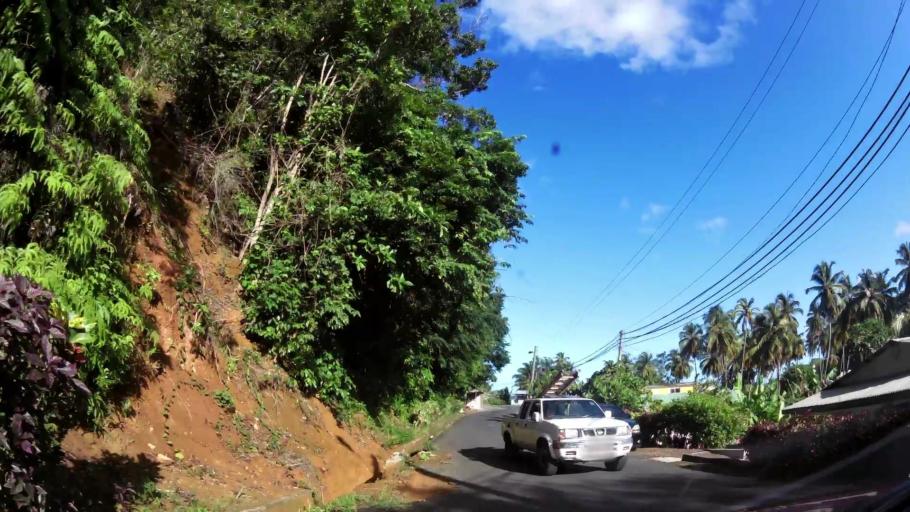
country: DM
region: Saint Andrew
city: Calibishie
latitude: 15.5919
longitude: -61.3821
